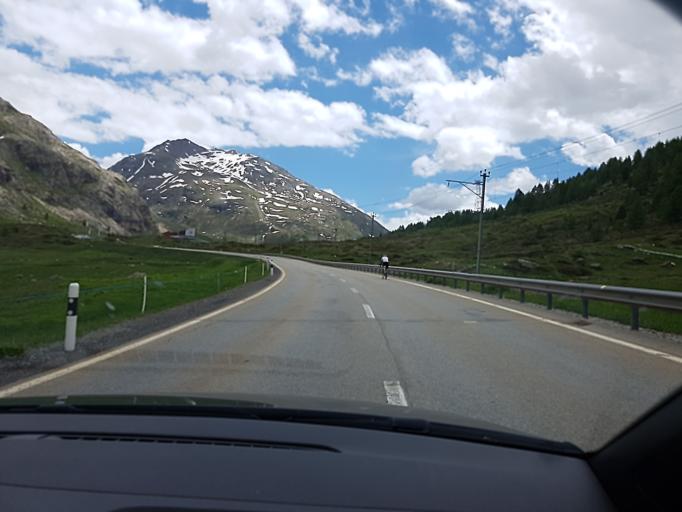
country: CH
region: Grisons
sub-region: Maloja District
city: Pontresina
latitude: 46.4434
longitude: 9.9739
